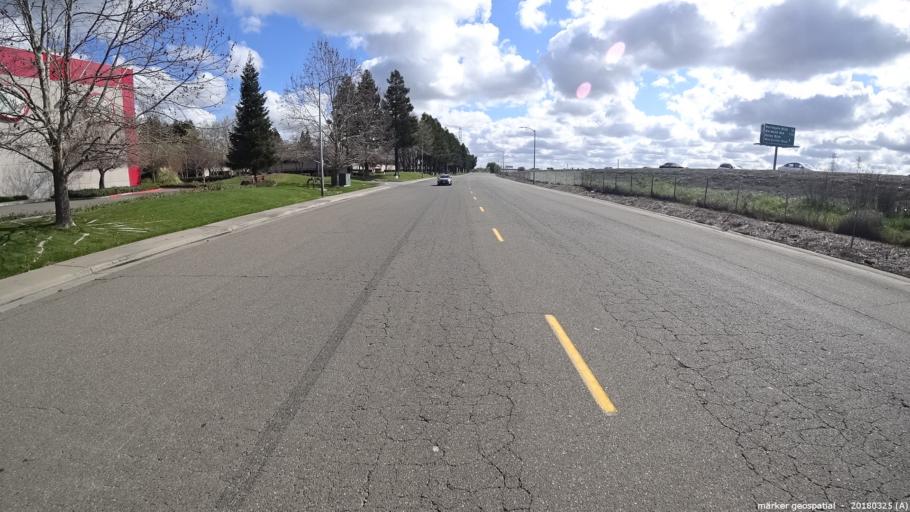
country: US
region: California
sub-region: Sacramento County
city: Sacramento
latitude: 38.6398
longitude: -121.4881
